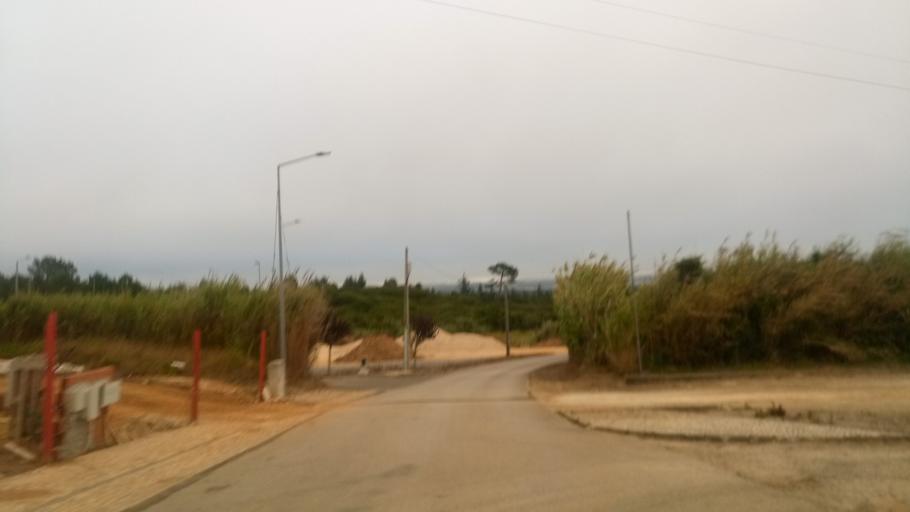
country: PT
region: Leiria
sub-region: Caldas da Rainha
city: Caldas da Rainha
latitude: 39.4595
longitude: -9.1891
